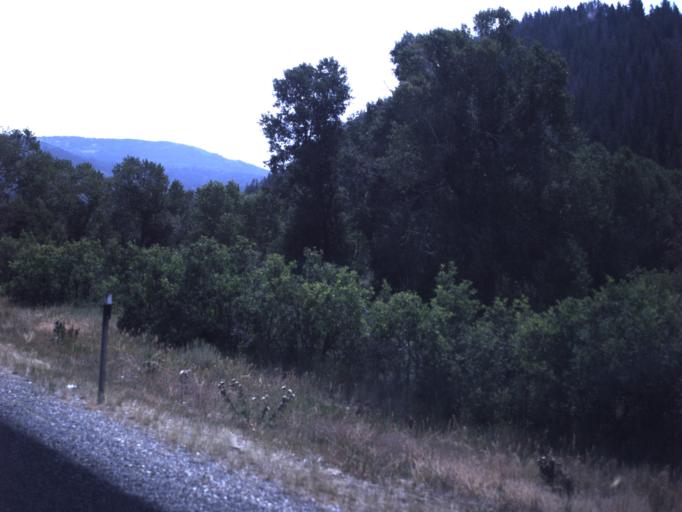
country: US
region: Utah
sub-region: Summit County
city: Francis
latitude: 40.5588
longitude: -111.1208
